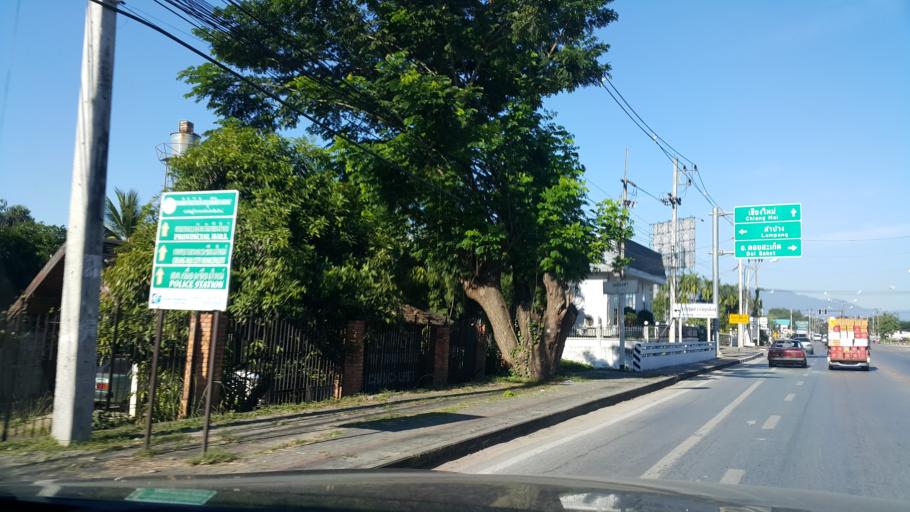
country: TH
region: Chiang Mai
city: San Kamphaeng
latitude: 18.7704
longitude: 99.0697
